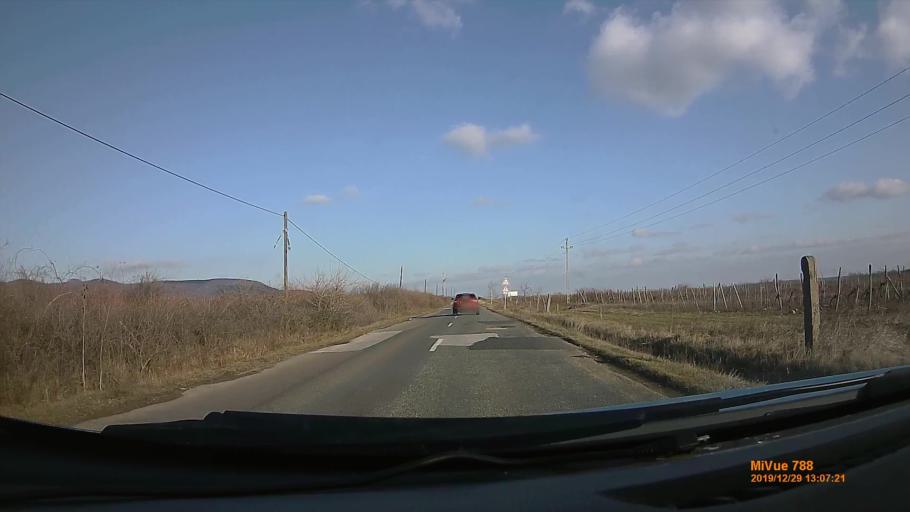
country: HU
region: Heves
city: Abasar
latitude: 47.8113
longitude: 20.0419
